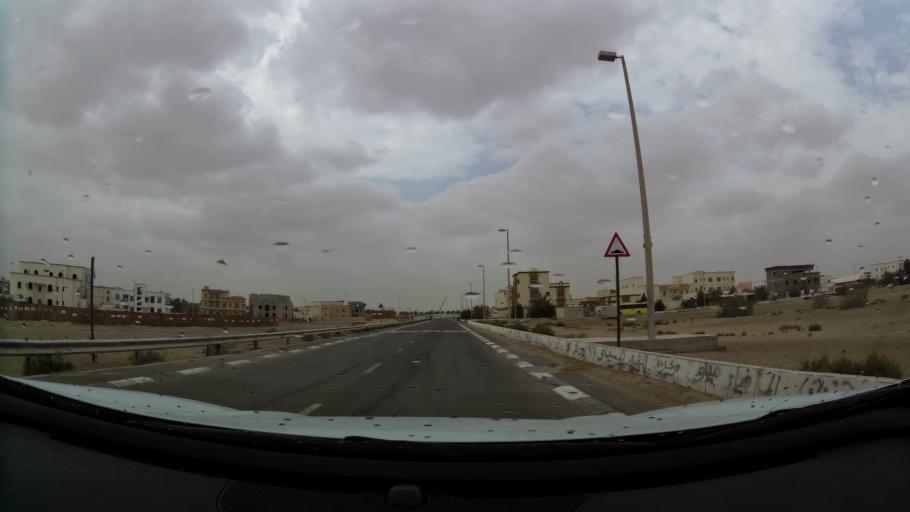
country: AE
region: Abu Dhabi
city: Abu Dhabi
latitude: 24.3288
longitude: 54.6350
